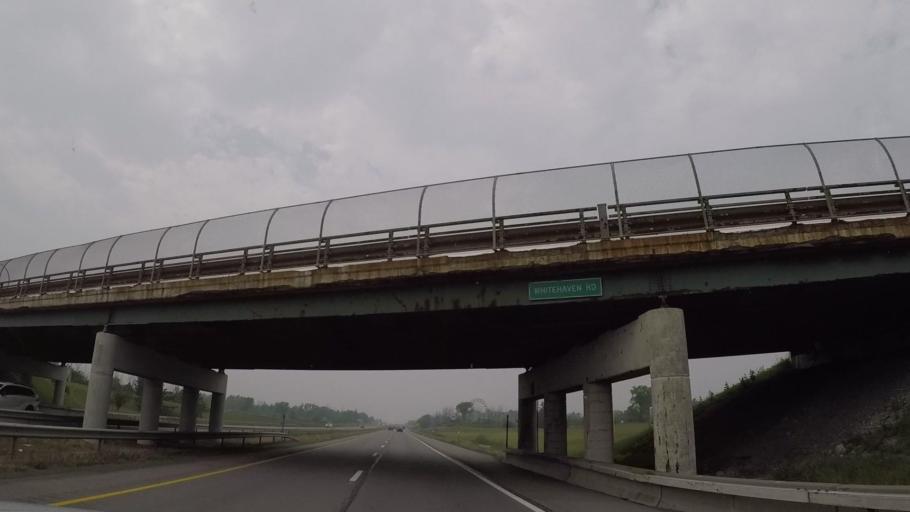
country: US
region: New York
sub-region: Erie County
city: Grandyle Village
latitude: 43.0215
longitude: -78.9743
